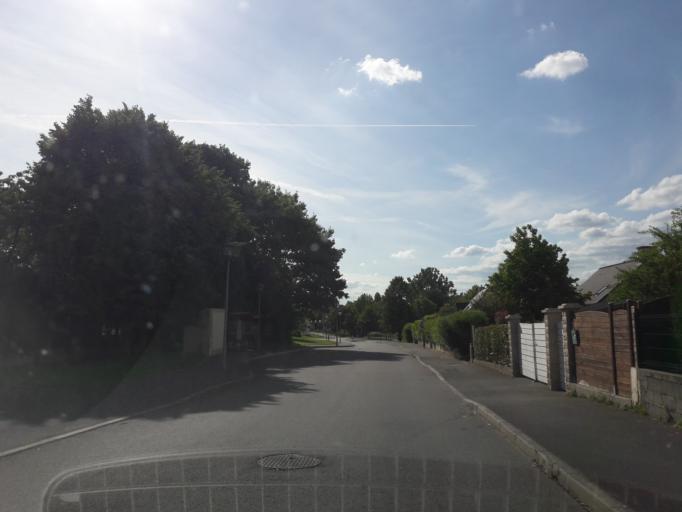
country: FR
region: Brittany
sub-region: Departement d'Ille-et-Vilaine
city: Nouvoitou
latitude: 48.0413
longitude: -1.5528
